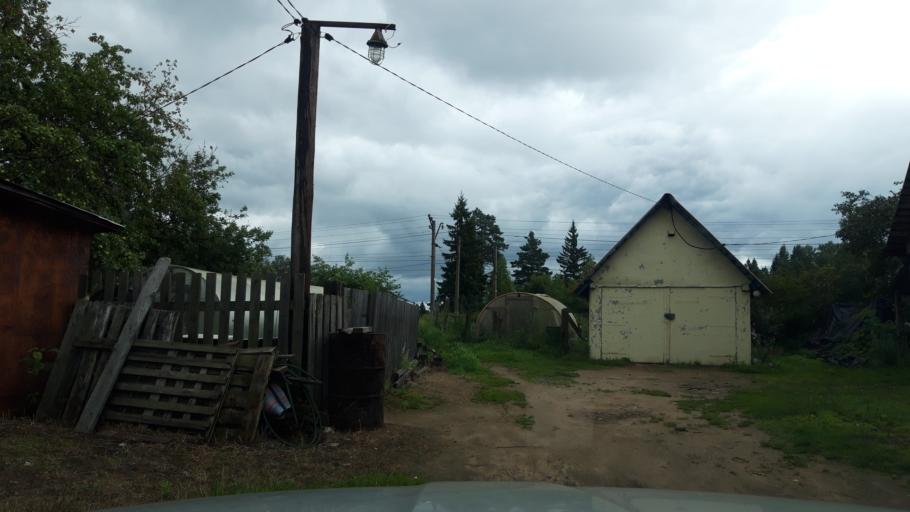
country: RU
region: Moskovskaya
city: Povarovo
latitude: 56.0604
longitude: 37.0798
